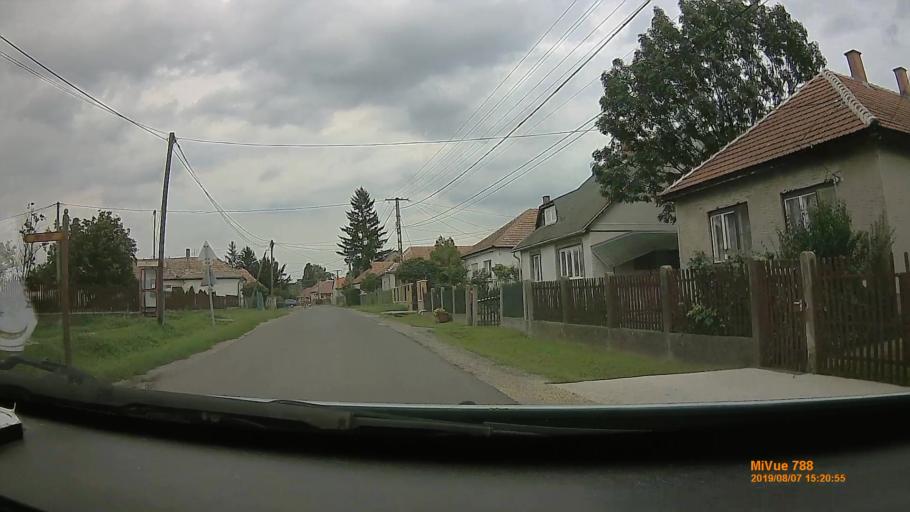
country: HU
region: Borsod-Abauj-Zemplen
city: Encs
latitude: 48.3571
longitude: 21.1511
